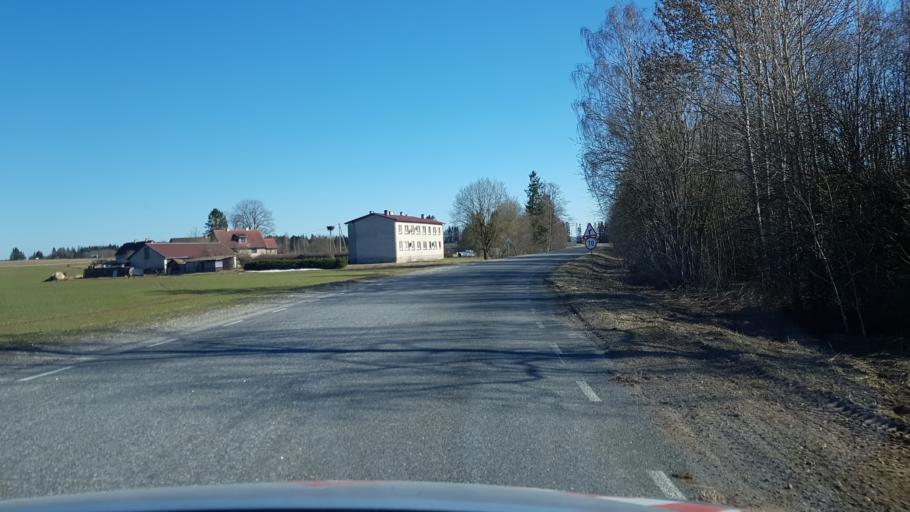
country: EE
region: Laeaene-Virumaa
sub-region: Someru vald
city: Someru
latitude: 59.3700
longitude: 26.4491
